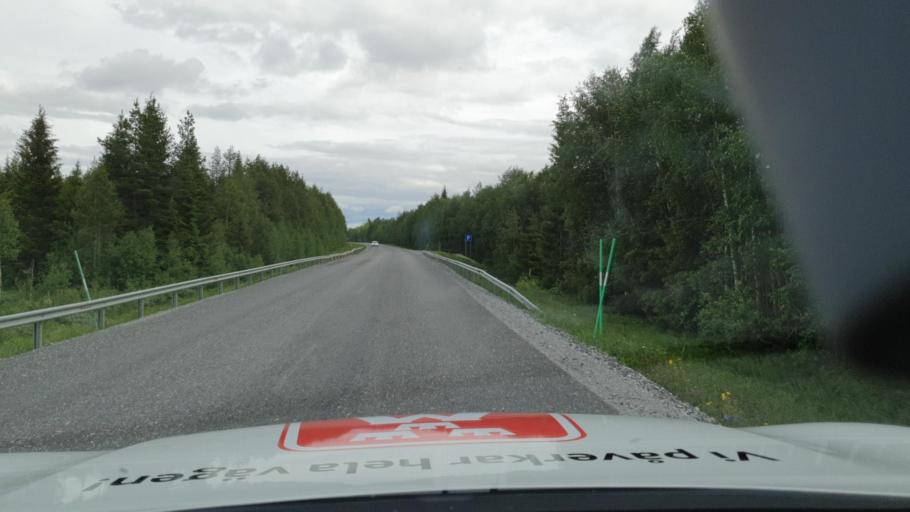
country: SE
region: Vaesterbotten
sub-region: Dorotea Kommun
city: Dorotea
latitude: 64.2295
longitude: 16.8180
